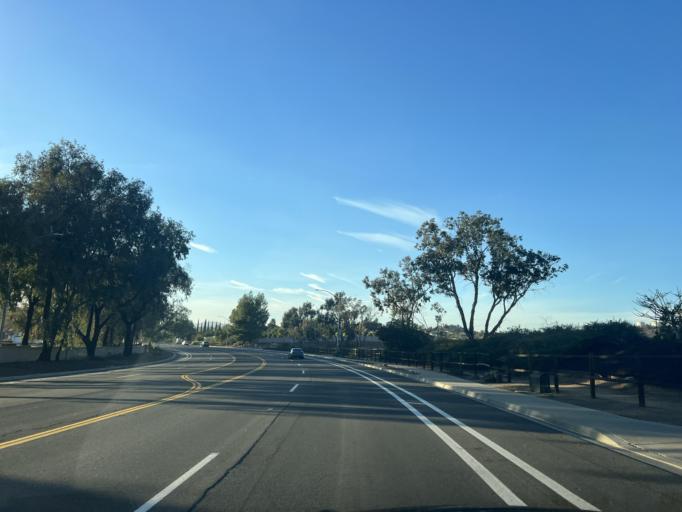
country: US
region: California
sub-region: San Diego County
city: Poway
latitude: 33.0176
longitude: -117.0252
